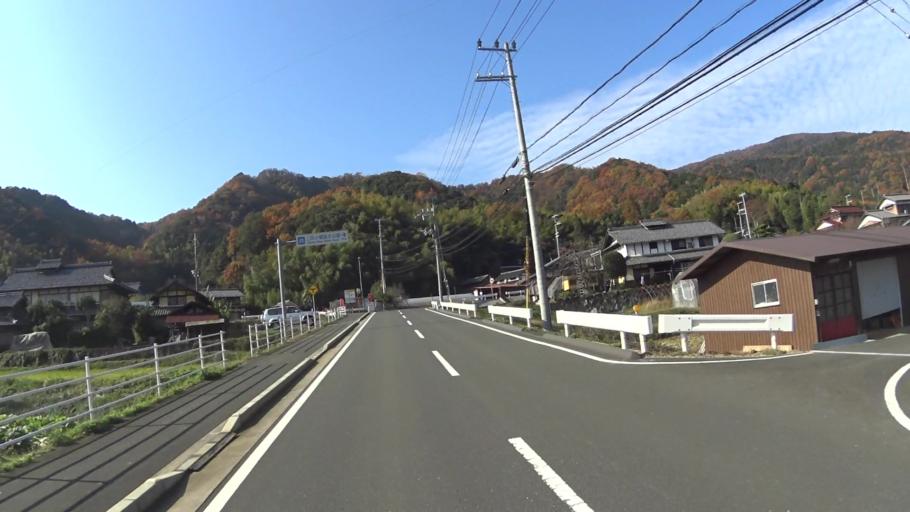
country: JP
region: Kyoto
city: Maizuru
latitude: 35.5214
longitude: 135.3907
